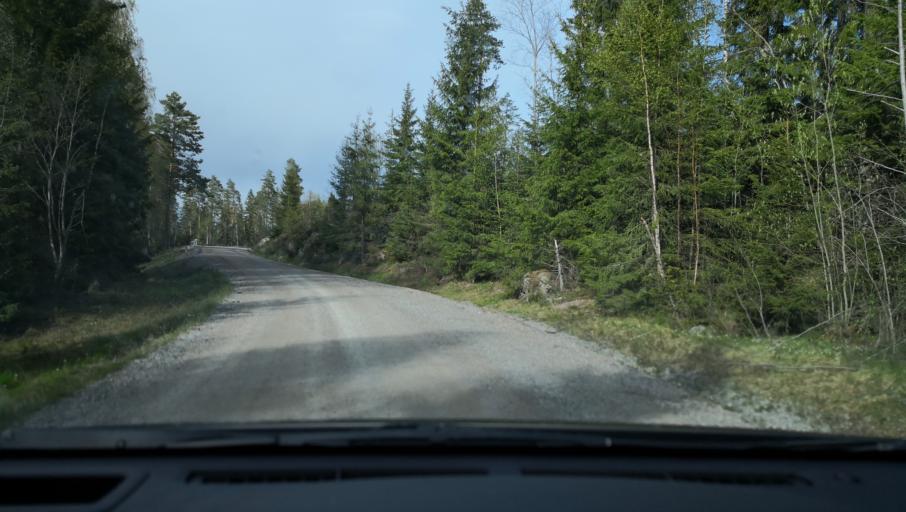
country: SE
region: Vaestmanland
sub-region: Fagersta Kommun
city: Fagersta
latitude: 60.1592
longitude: 15.7147
